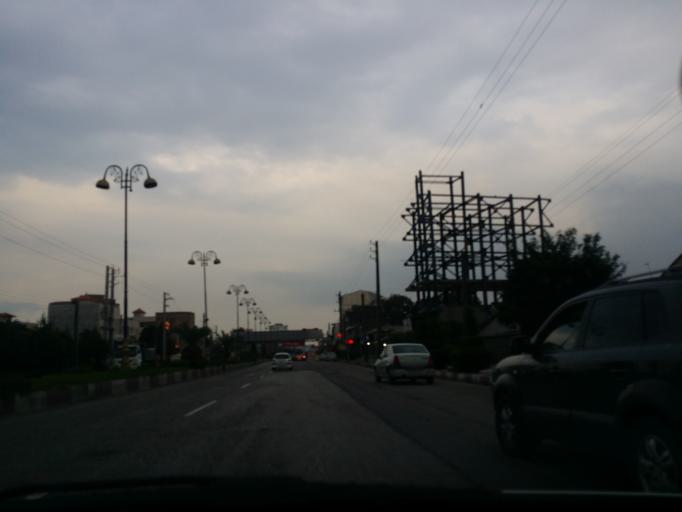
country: IR
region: Mazandaran
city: `Abbasabad
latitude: 36.7265
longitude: 51.1159
